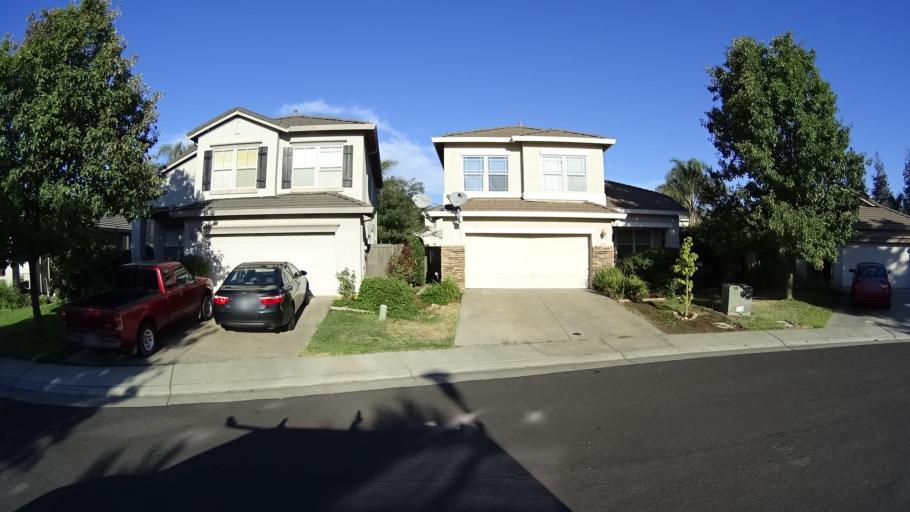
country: US
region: California
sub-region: Sacramento County
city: Laguna
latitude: 38.4043
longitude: -121.4756
